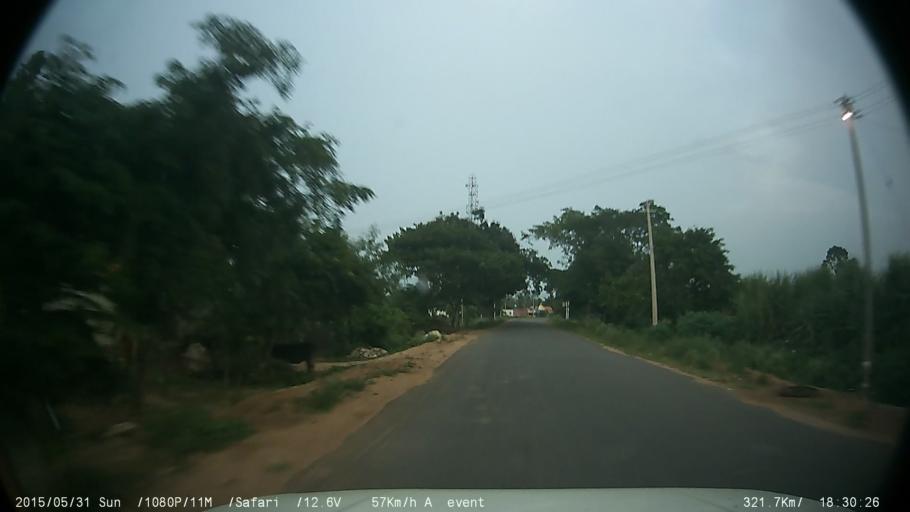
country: IN
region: Karnataka
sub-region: Mysore
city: Nanjangud
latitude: 12.1258
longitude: 76.7380
